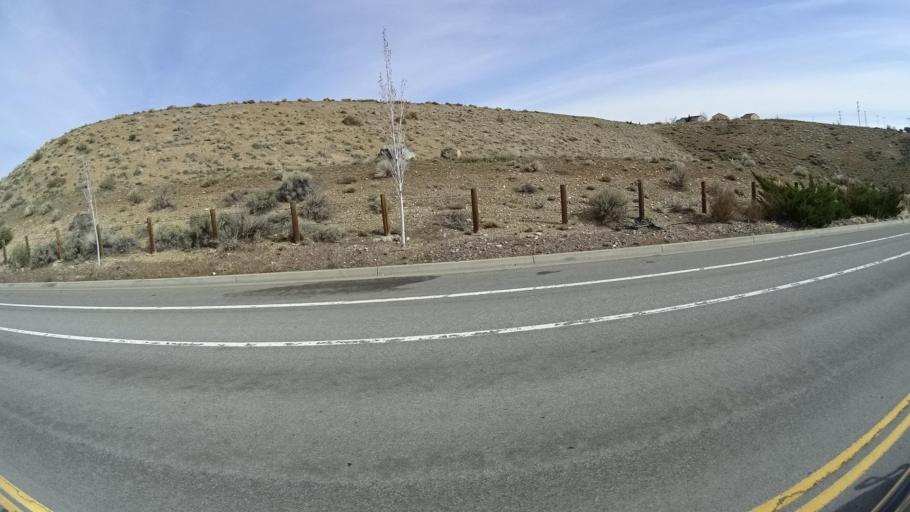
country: US
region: Nevada
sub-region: Washoe County
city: Reno
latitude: 39.5420
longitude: -119.8672
